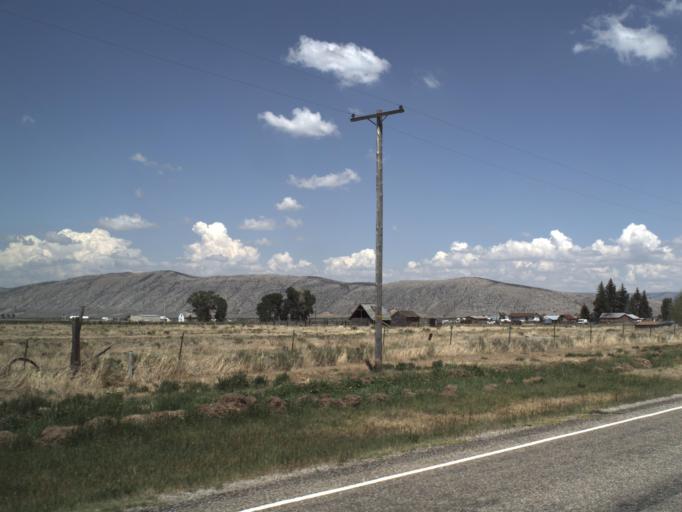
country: US
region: Utah
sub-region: Rich County
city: Randolph
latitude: 41.5241
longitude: -111.1724
